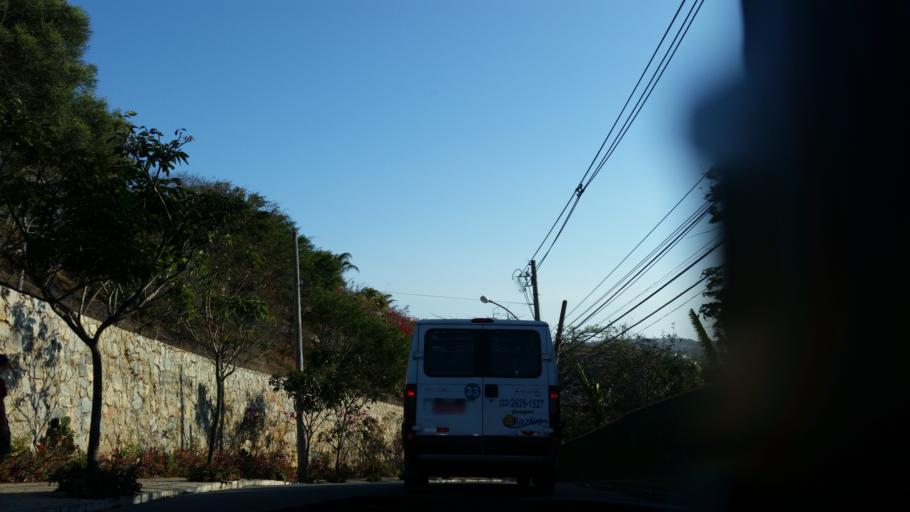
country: BR
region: Rio de Janeiro
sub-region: Armacao De Buzios
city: Armacao de Buzios
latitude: -22.7487
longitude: -41.8797
